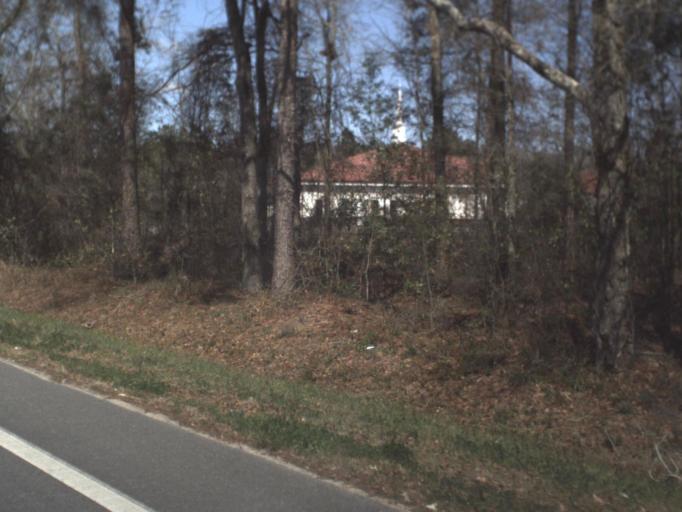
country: US
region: Florida
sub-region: Gadsden County
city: Gretna
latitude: 30.6462
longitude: -84.6792
